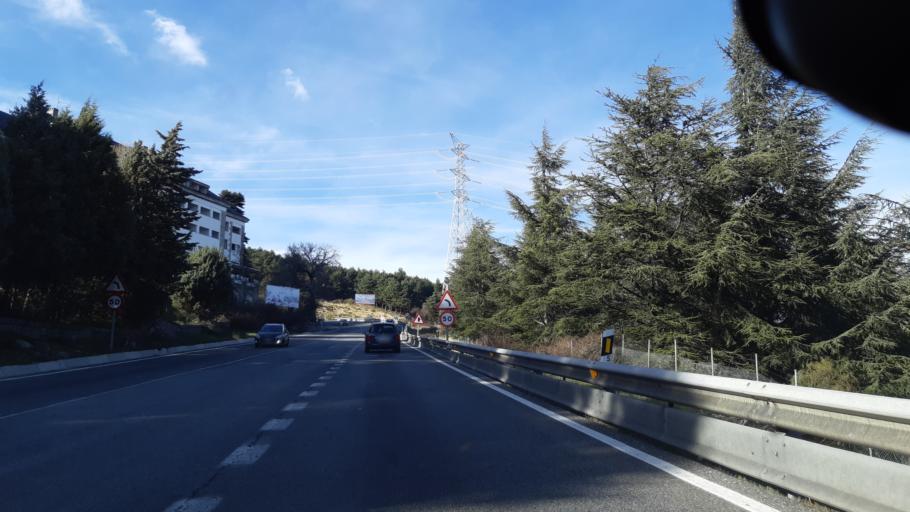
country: ES
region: Madrid
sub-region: Provincia de Madrid
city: Guadarrama
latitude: 40.7076
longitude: -4.1273
